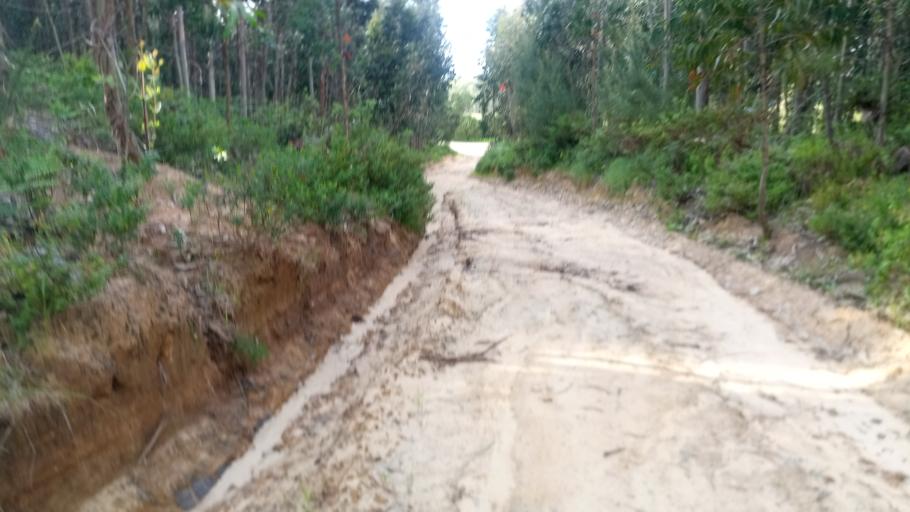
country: PT
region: Leiria
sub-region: Obidos
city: Obidos
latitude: 39.4016
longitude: -9.1938
